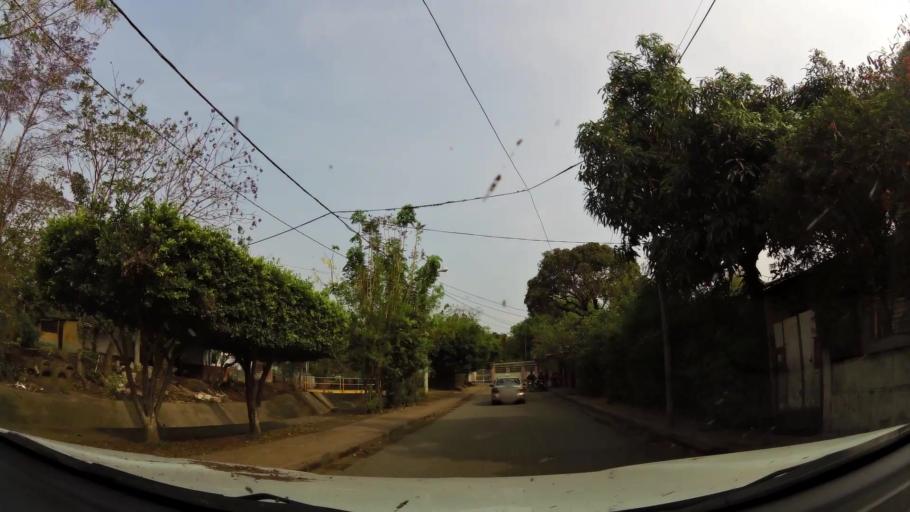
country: NI
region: Masaya
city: Masaya
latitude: 11.9694
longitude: -86.0858
